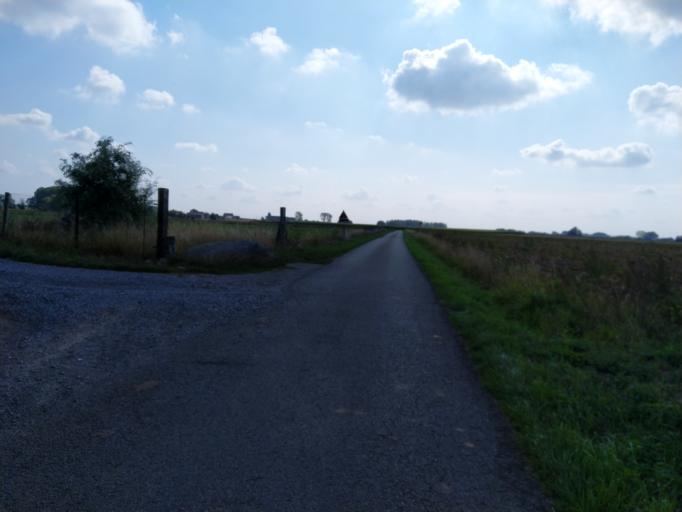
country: BE
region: Wallonia
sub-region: Province du Hainaut
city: Jurbise
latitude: 50.5586
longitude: 3.9668
